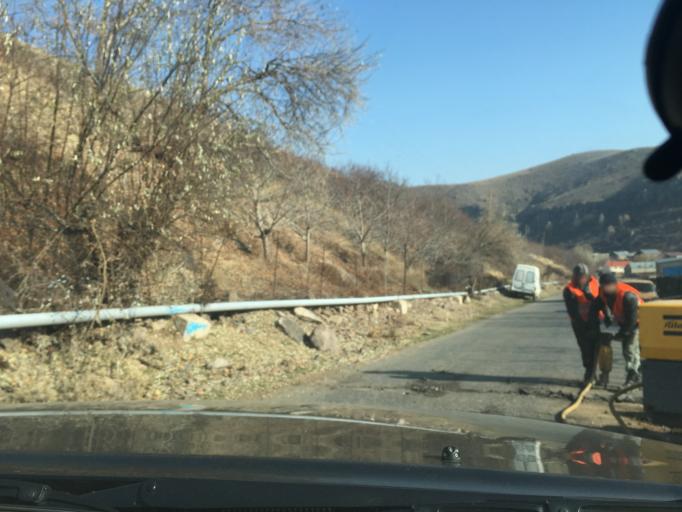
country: AM
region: Kotayk'i Marz
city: Bjni
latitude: 40.4454
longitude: 44.6332
